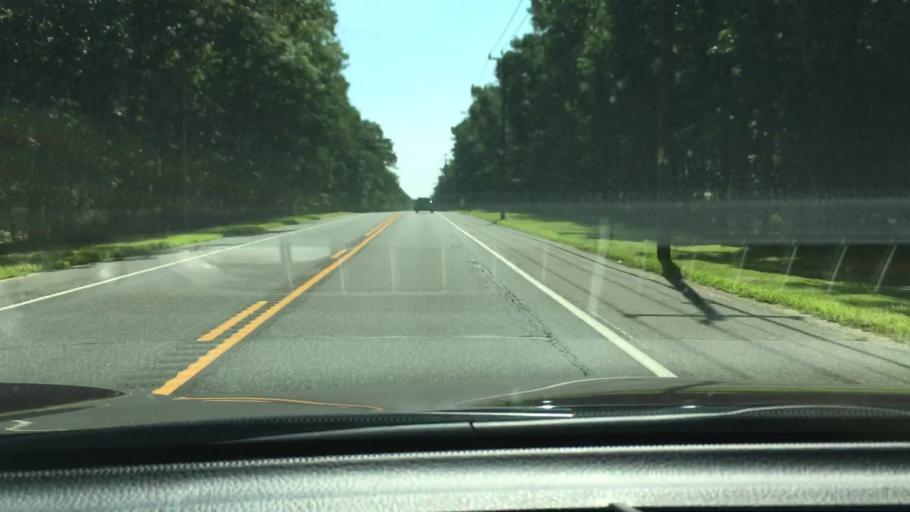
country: US
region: New Jersey
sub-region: Cumberland County
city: Millville
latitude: 39.3812
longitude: -74.9716
